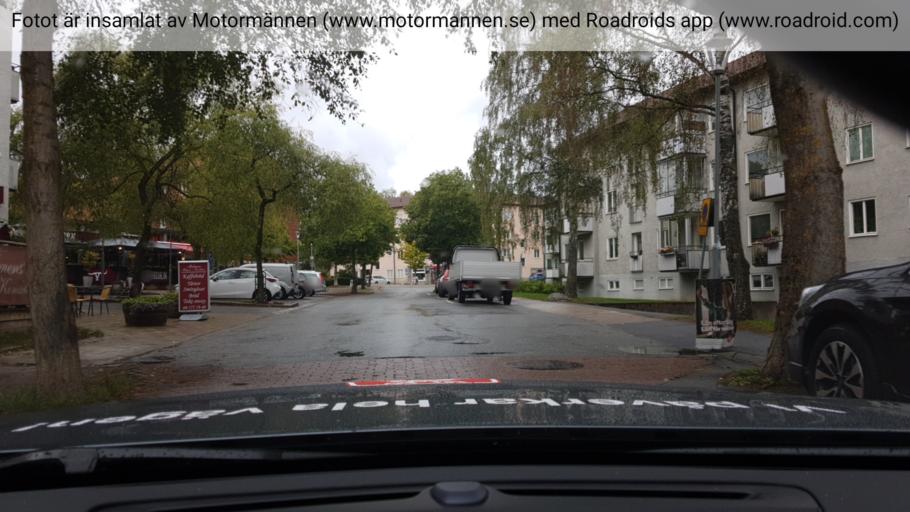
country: SE
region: Stockholm
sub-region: Haninge Kommun
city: Haninge
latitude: 59.1703
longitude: 18.1448
